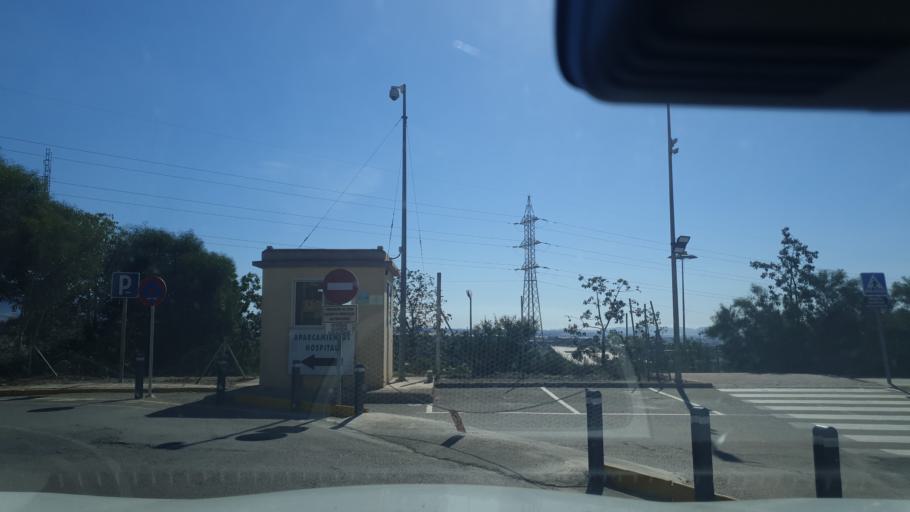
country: ES
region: Andalusia
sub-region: Provincia de Almeria
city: Huercal de Almeria
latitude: 36.8622
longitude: -2.4399
